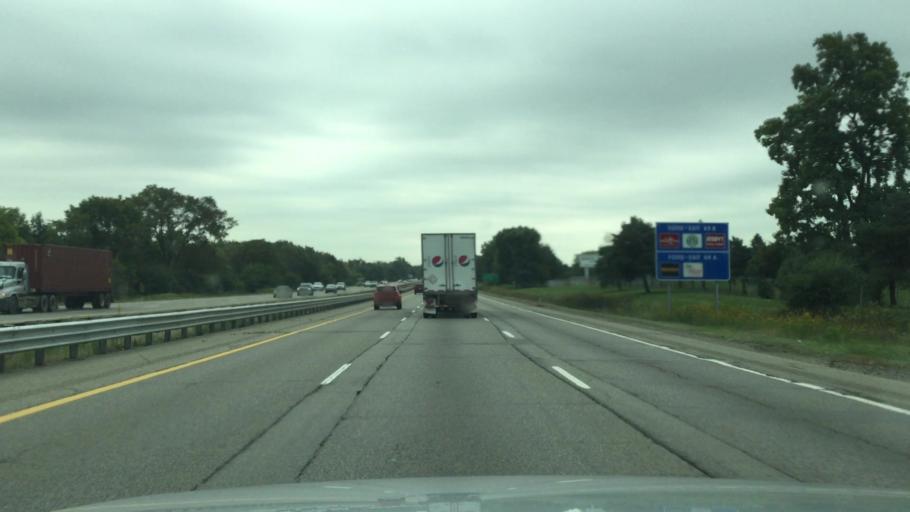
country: US
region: Michigan
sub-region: Oakland County
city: Troy
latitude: 42.5871
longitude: -83.1594
